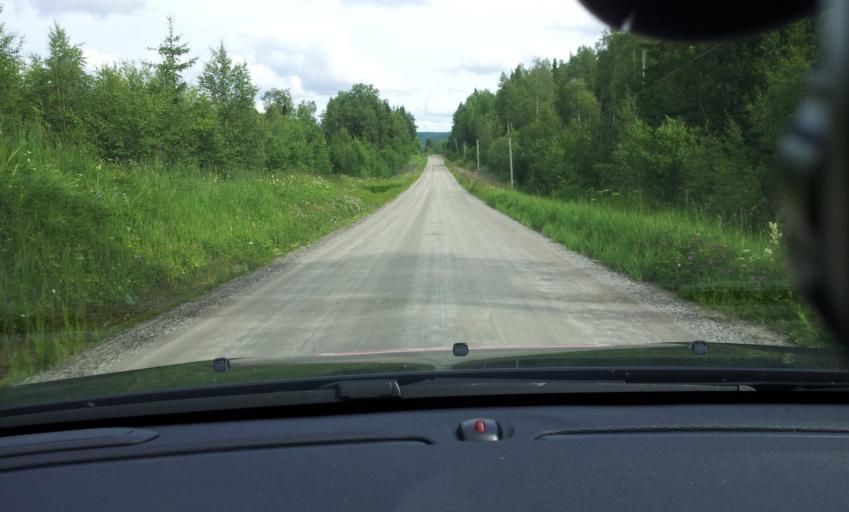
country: SE
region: Jaemtland
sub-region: OEstersunds Kommun
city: Brunflo
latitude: 62.9418
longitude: 14.9751
